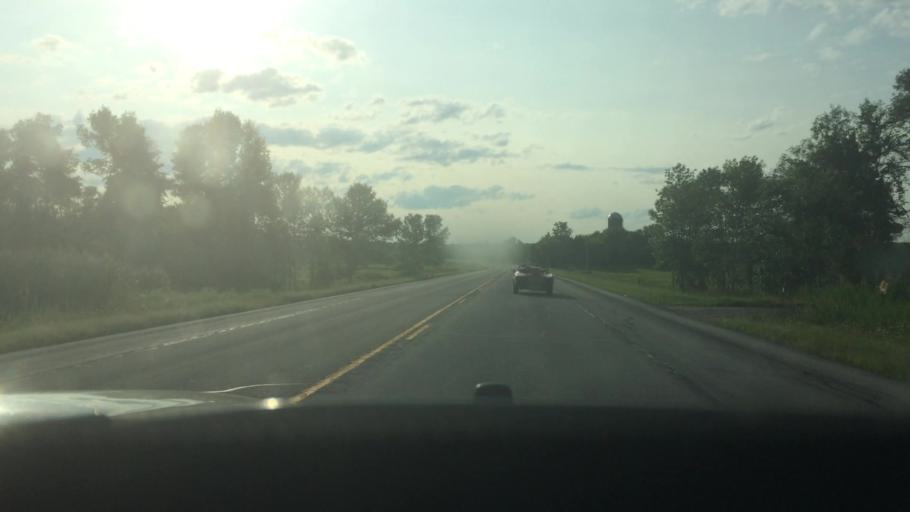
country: US
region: New York
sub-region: St. Lawrence County
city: Canton
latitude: 44.6345
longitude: -75.2568
